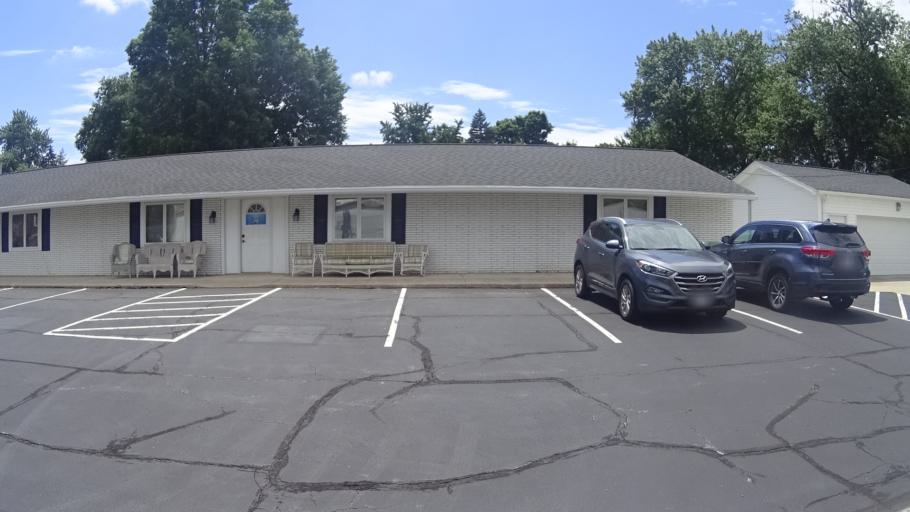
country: US
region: Ohio
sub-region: Erie County
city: Milan
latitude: 41.2984
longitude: -82.6073
